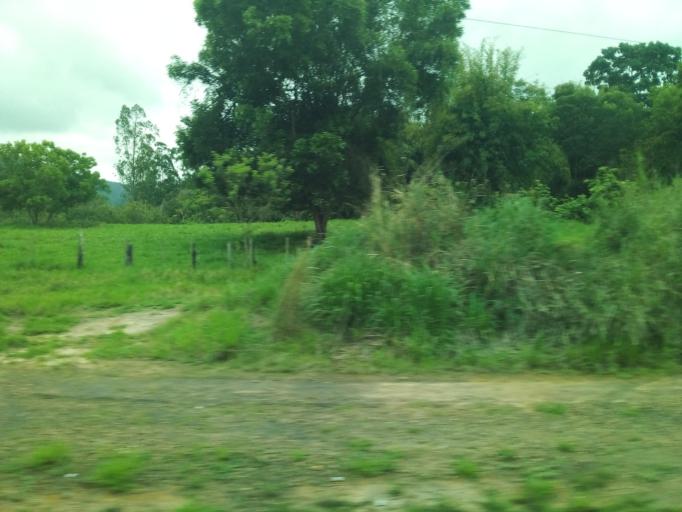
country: BR
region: Minas Gerais
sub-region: Rio Piracicaba
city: Rio Piracicaba
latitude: -19.9513
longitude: -43.1802
